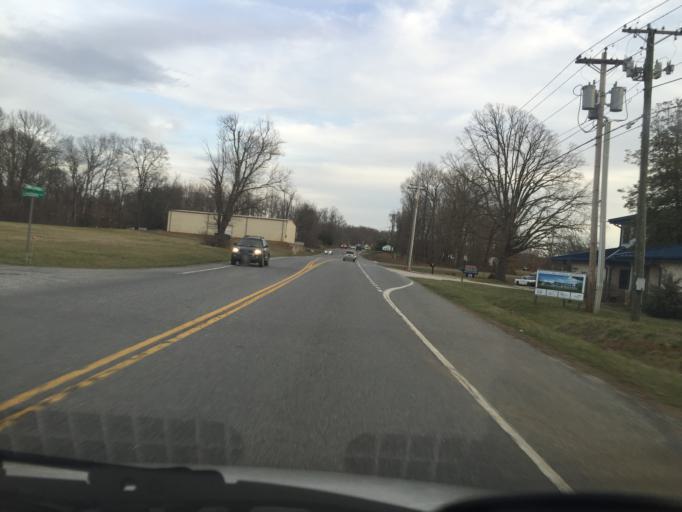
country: US
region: Virginia
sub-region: Bedford County
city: Forest
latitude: 37.3602
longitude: -79.2852
